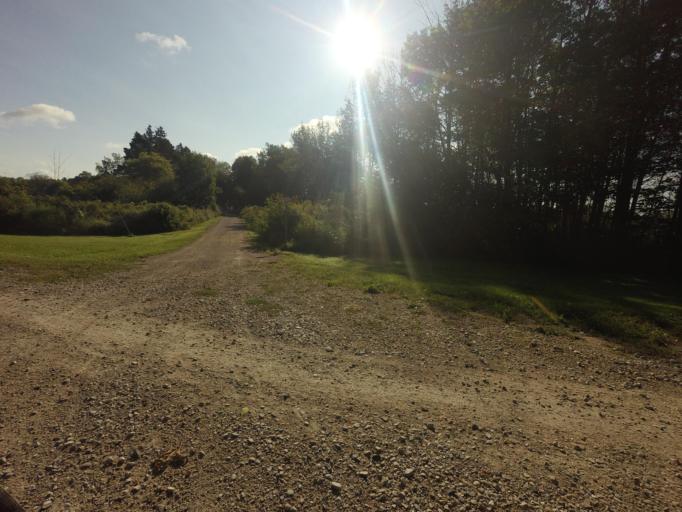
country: CA
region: Ontario
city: Huron East
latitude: 43.7383
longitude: -81.4473
